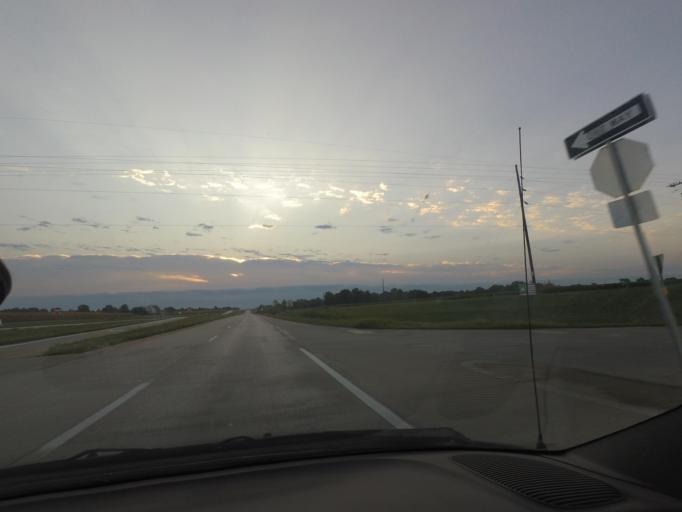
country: US
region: Missouri
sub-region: Macon County
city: Macon
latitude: 39.7507
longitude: -92.3834
